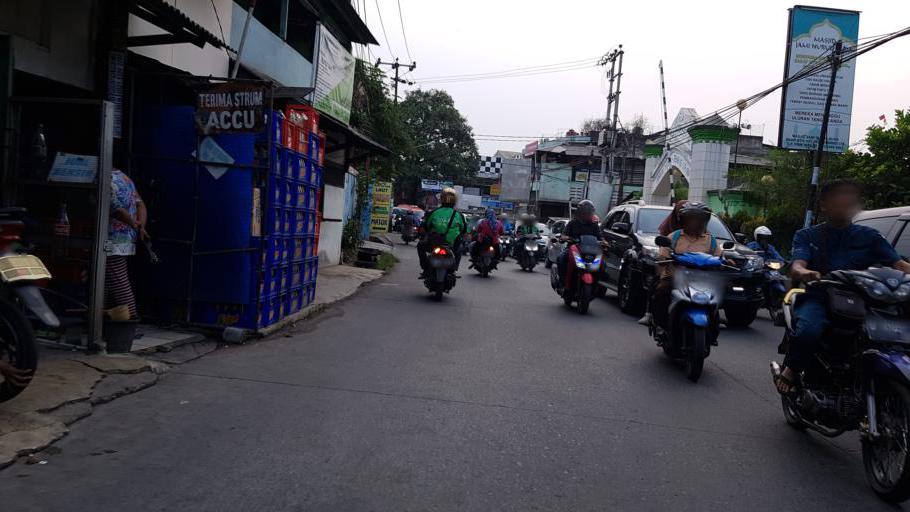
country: ID
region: West Java
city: Bekasi
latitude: -6.2832
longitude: 106.9288
